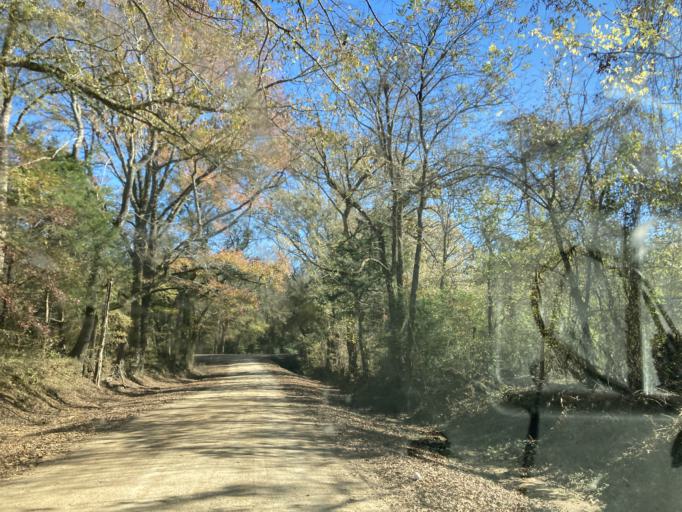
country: US
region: Mississippi
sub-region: Hinds County
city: Lynchburg
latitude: 32.5822
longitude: -90.5709
